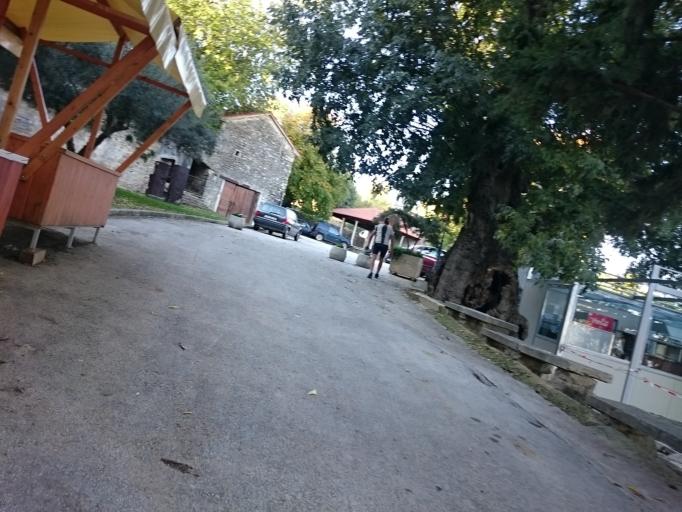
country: HR
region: Istarska
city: Buje
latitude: 45.3792
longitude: 13.7233
